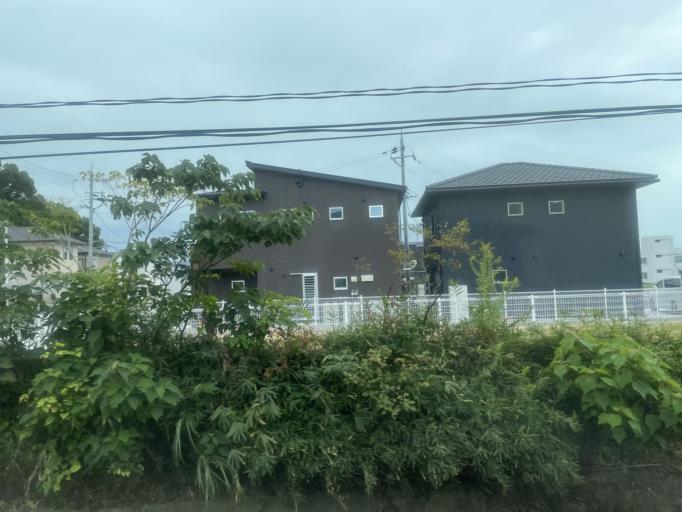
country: JP
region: Wakayama
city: Wakayama-shi
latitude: 34.2683
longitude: 135.2329
